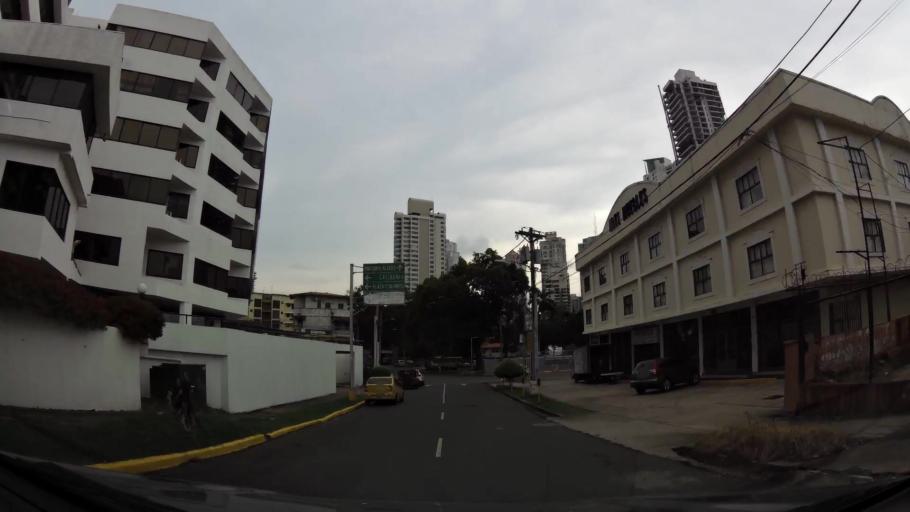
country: PA
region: Panama
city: Panama
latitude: 8.9782
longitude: -79.5315
